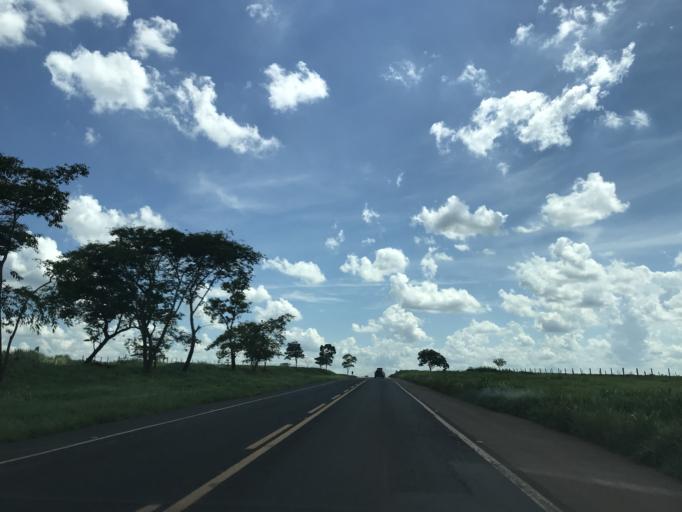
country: BR
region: Sao Paulo
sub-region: Nova Granada
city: Nova Granada
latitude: -20.4517
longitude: -49.2846
